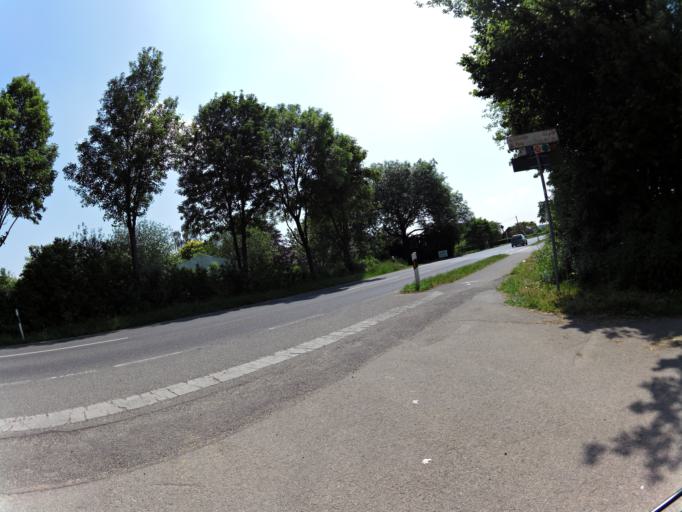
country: DE
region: North Rhine-Westphalia
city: Julich
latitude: 50.9375
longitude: 6.3385
